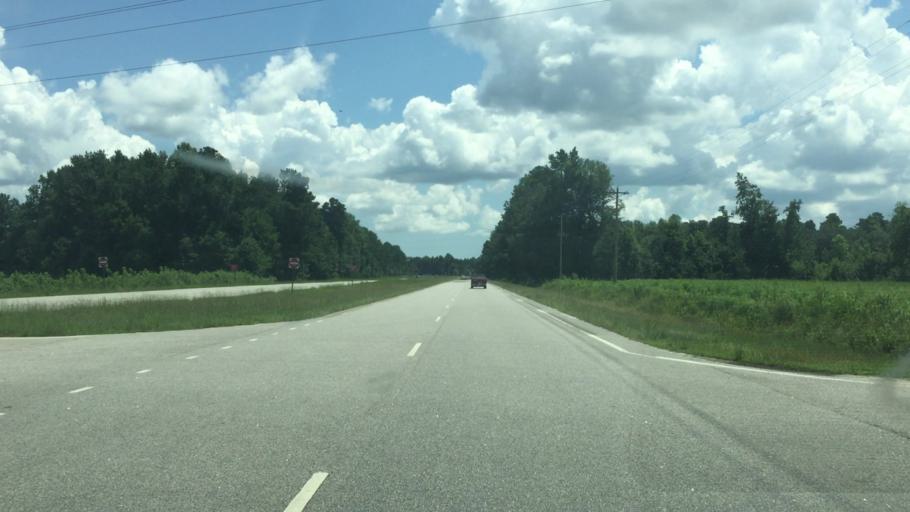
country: US
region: South Carolina
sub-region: Horry County
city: Loris
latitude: 34.0251
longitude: -78.7991
